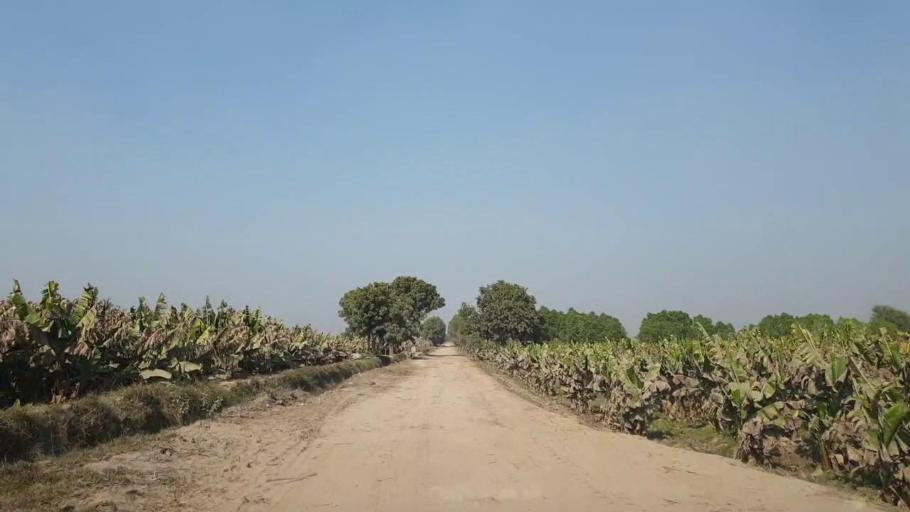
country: PK
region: Sindh
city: Tando Allahyar
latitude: 25.5082
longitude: 68.8221
